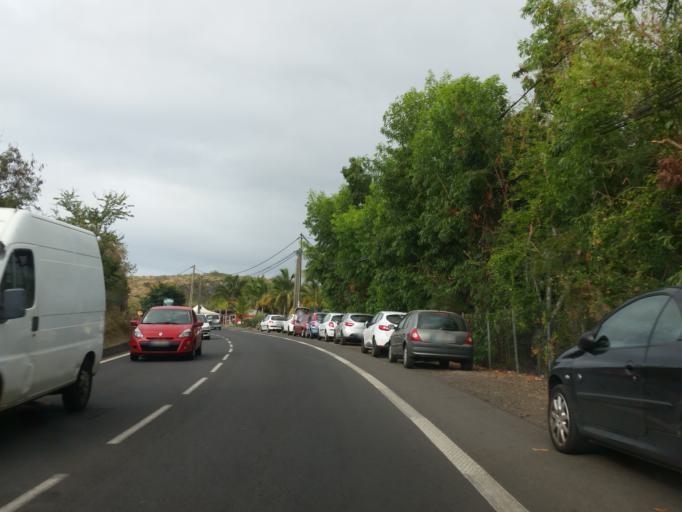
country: RE
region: Reunion
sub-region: Reunion
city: Saint-Paul
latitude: -21.0460
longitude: 55.2398
